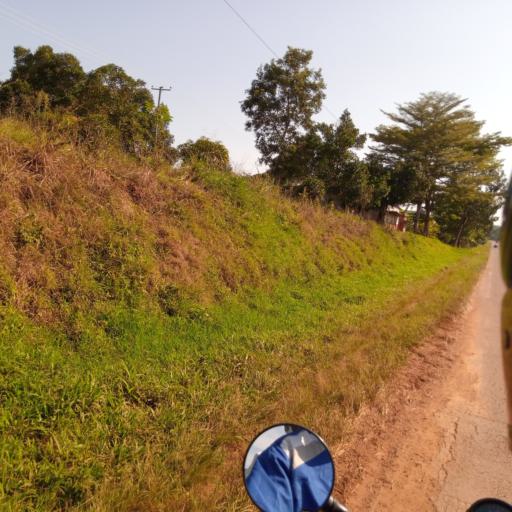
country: UG
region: Central Region
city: Masaka
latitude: -0.4548
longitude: 31.6668
